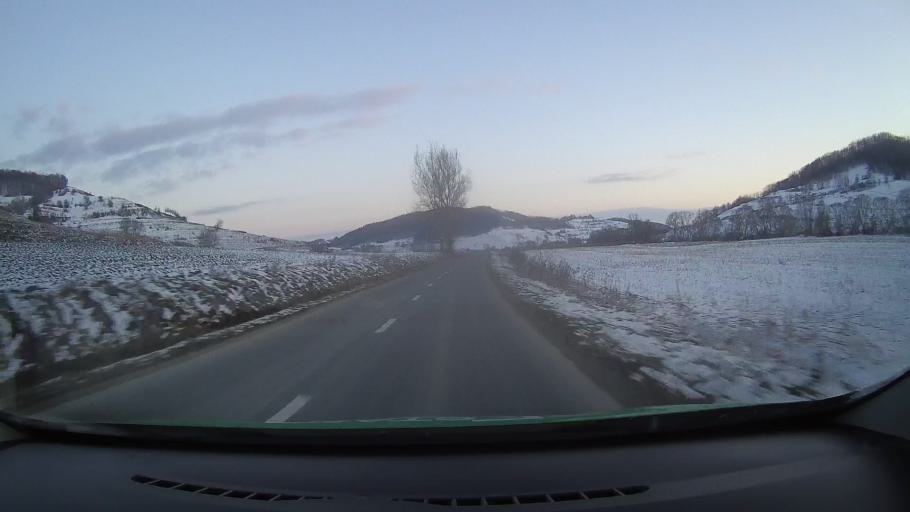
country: RO
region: Sibiu
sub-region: Comuna Alma
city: Alma
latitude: 46.1988
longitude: 24.4695
